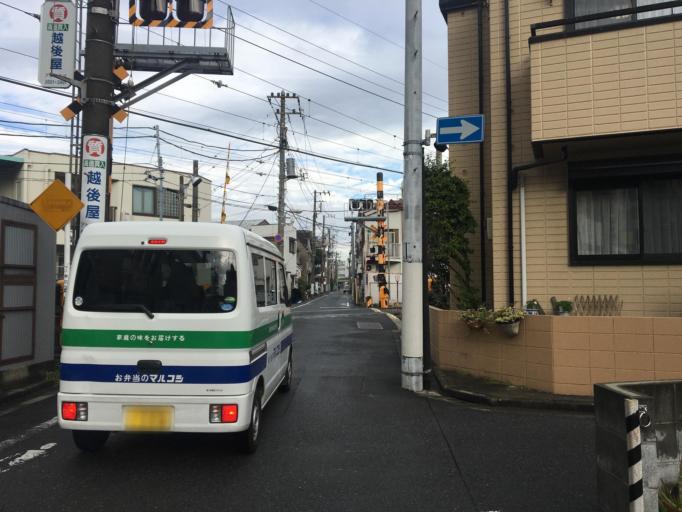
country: JP
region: Tokyo
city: Urayasu
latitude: 35.6985
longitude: 139.8328
